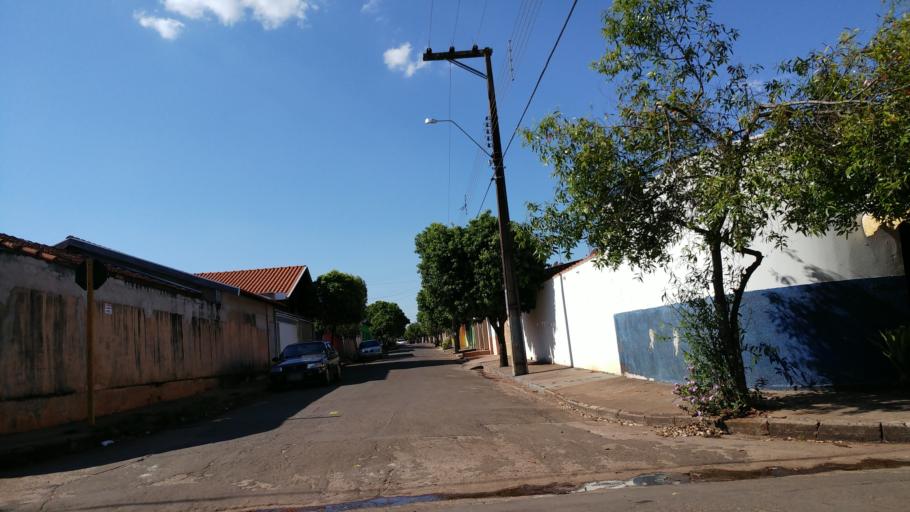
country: BR
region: Sao Paulo
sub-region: Paraguacu Paulista
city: Paraguacu Paulista
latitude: -22.4346
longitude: -50.5809
